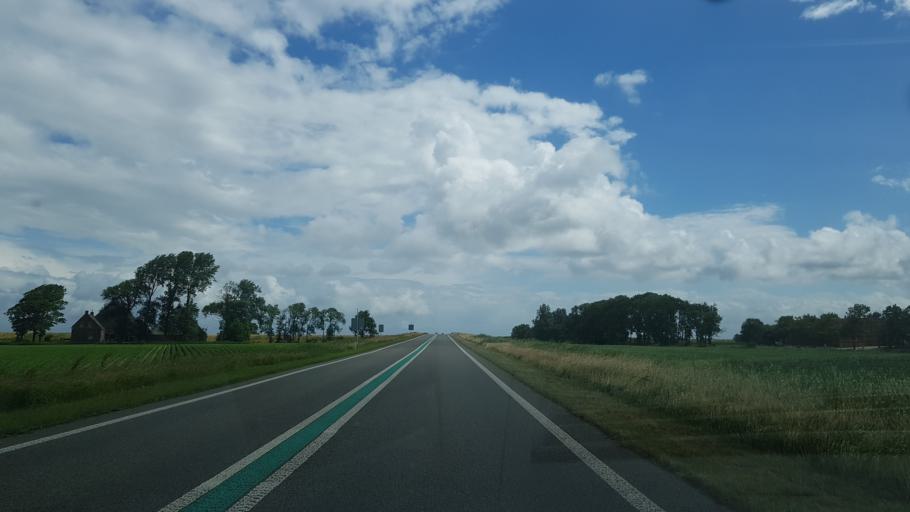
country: NL
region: Friesland
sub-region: Gemeente Dongeradeel
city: Anjum
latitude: 53.3821
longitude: 6.1287
